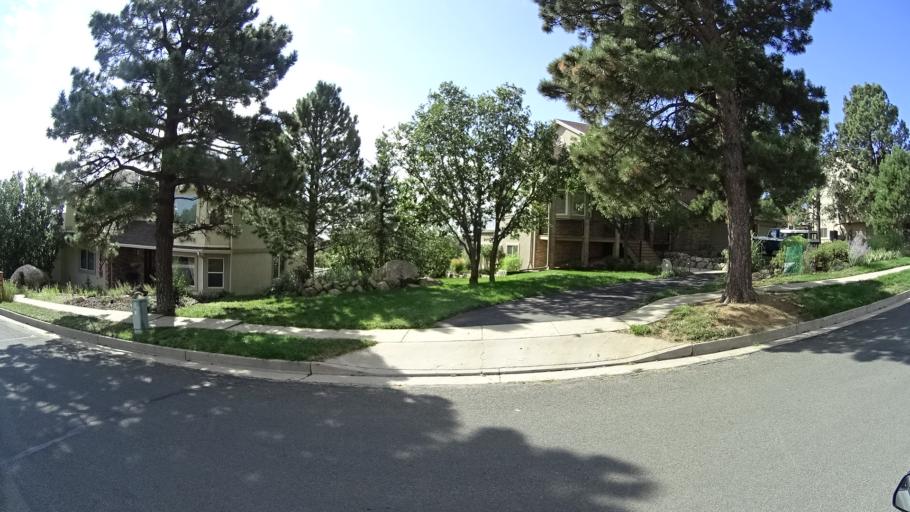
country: US
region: Colorado
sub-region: El Paso County
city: Fort Carson
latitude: 38.7666
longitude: -104.8317
